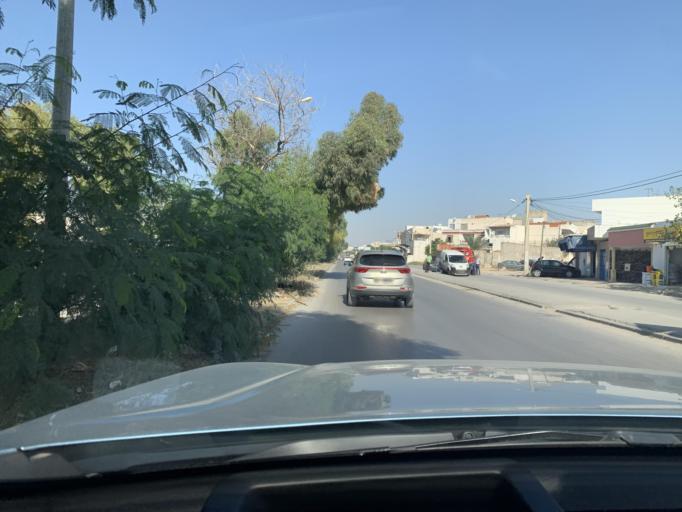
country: TN
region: Manouba
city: Manouba
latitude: 36.8204
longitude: 10.1242
